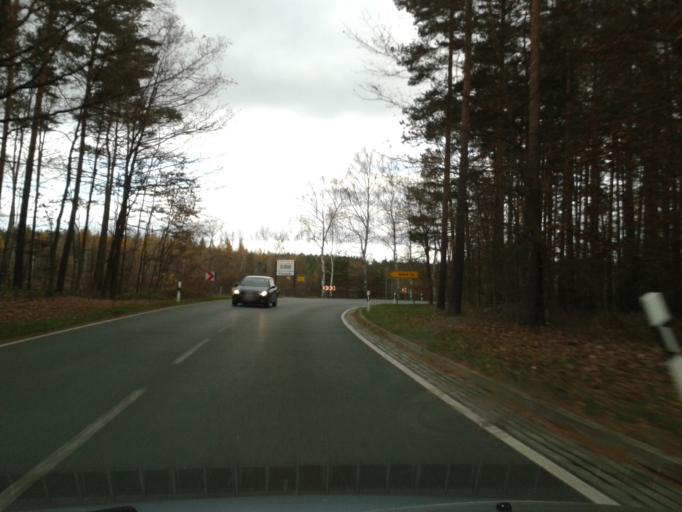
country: DE
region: Thuringia
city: Hainspitz
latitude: 50.9267
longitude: 11.8303
